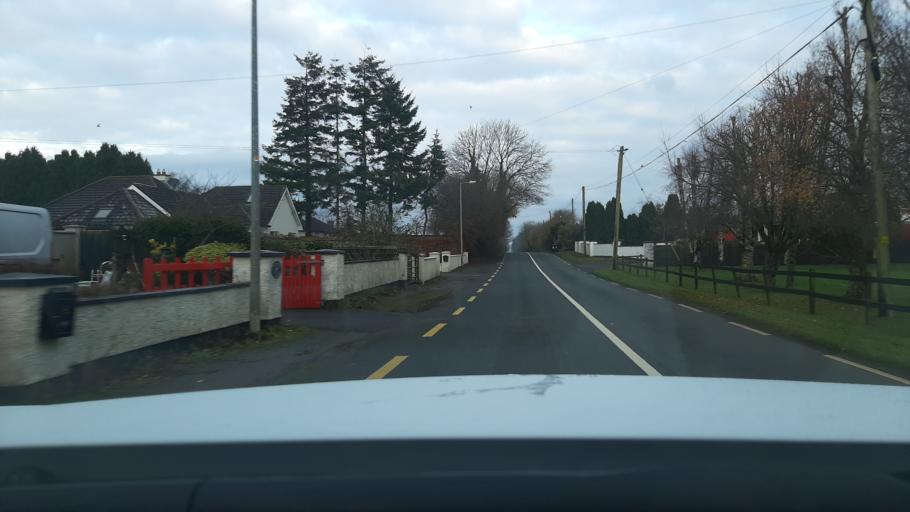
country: IE
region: Leinster
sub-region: Kildare
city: Rathangan
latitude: 53.2347
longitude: -7.0100
